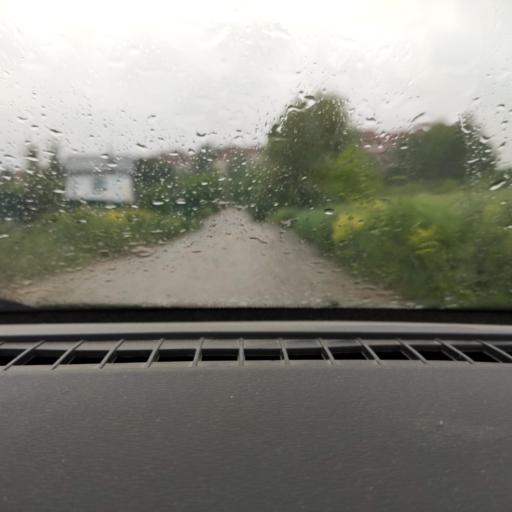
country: RU
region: Perm
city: Perm
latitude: 58.0335
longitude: 56.3613
